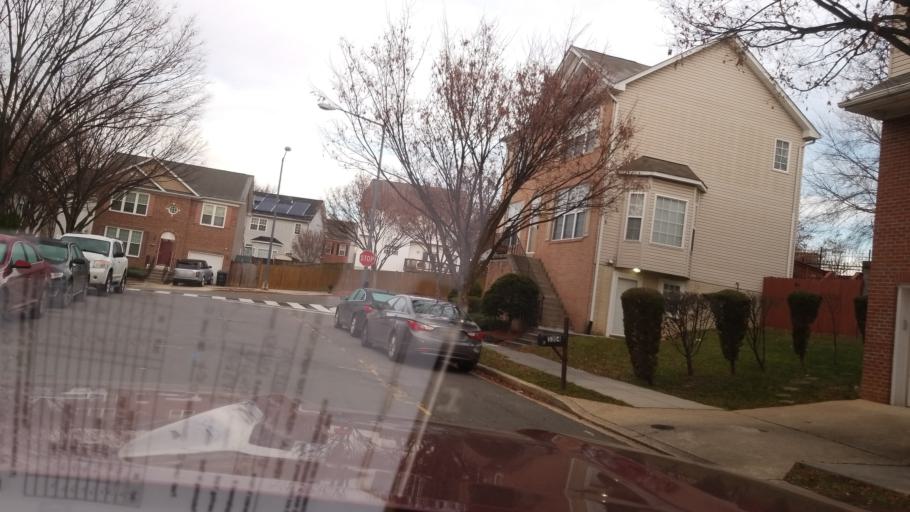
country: US
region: Maryland
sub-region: Prince George's County
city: Glassmanor
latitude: 38.8410
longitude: -76.9955
